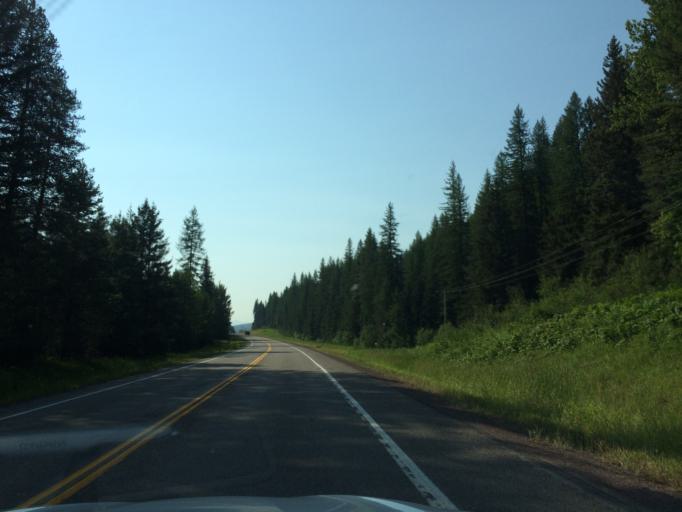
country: US
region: Montana
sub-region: Flathead County
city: Columbia Falls
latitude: 48.4104
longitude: -113.7240
